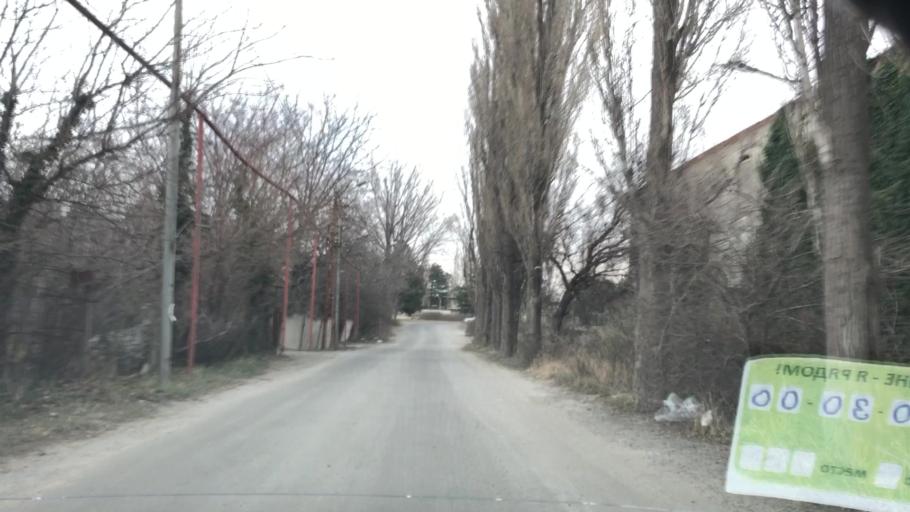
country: GE
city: Didi Lilo
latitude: 41.7012
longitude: 44.9267
